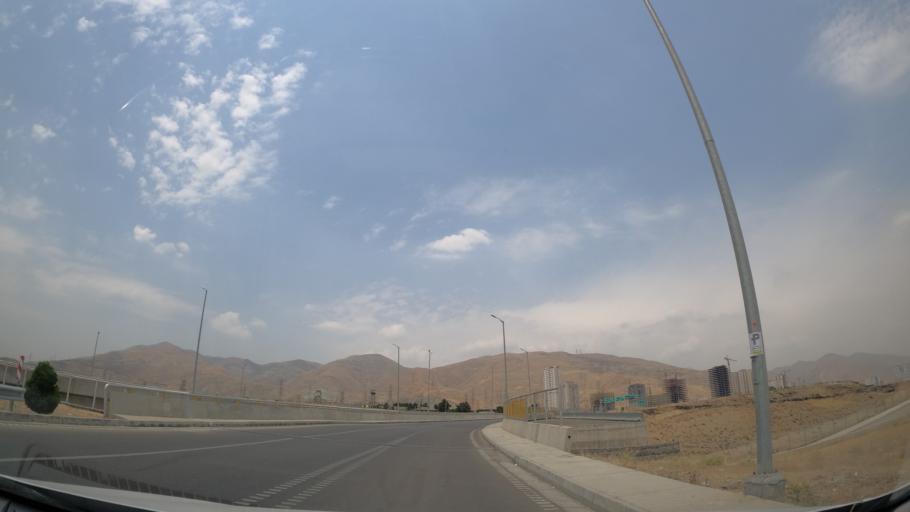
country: IR
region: Tehran
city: Shahr-e Qods
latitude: 35.7454
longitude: 51.1280
